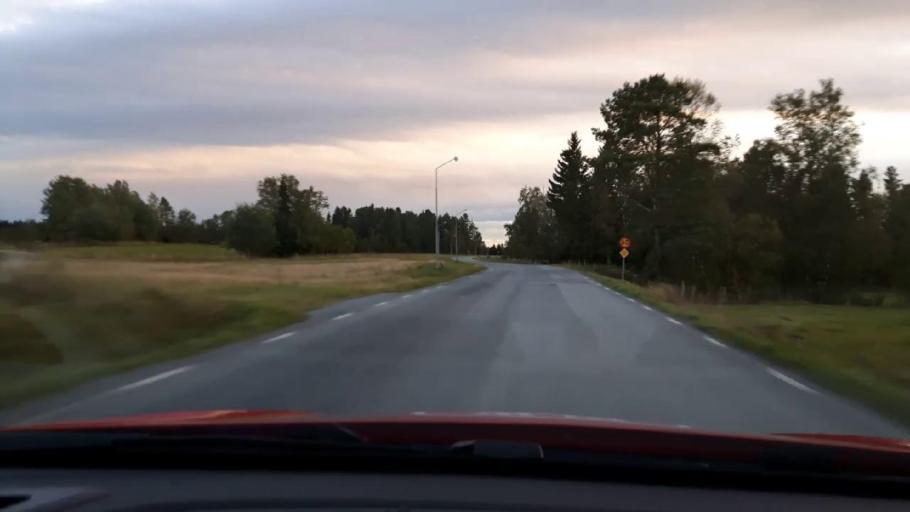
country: SE
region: Jaemtland
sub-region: OEstersunds Kommun
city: Ostersund
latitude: 63.0567
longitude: 14.4506
